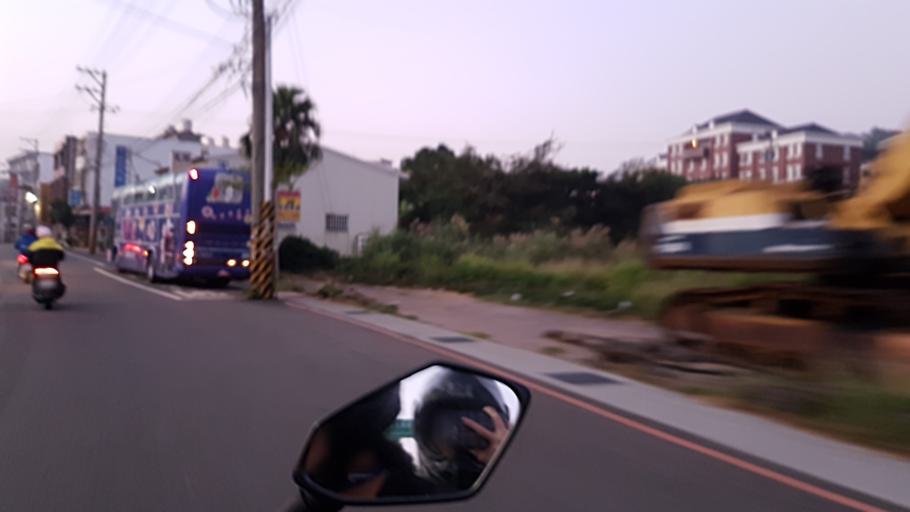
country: TW
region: Taiwan
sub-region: Hsinchu
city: Hsinchu
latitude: 24.7787
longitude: 120.9672
